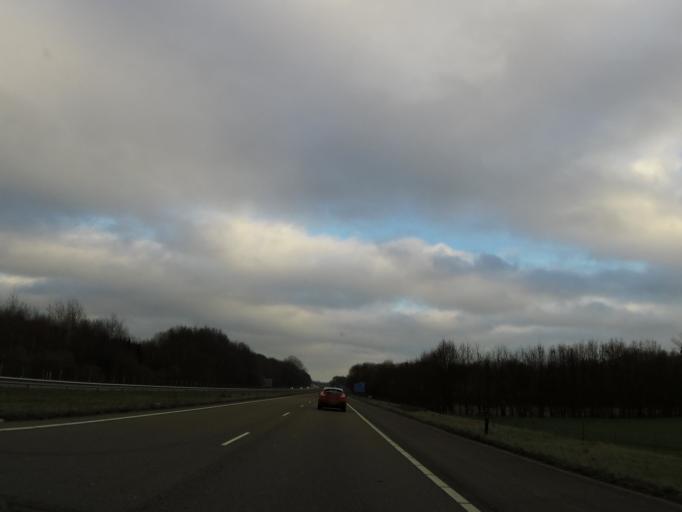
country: NL
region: Limburg
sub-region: Gemeente Meerssen
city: Meerssen
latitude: 50.8778
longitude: 5.7572
